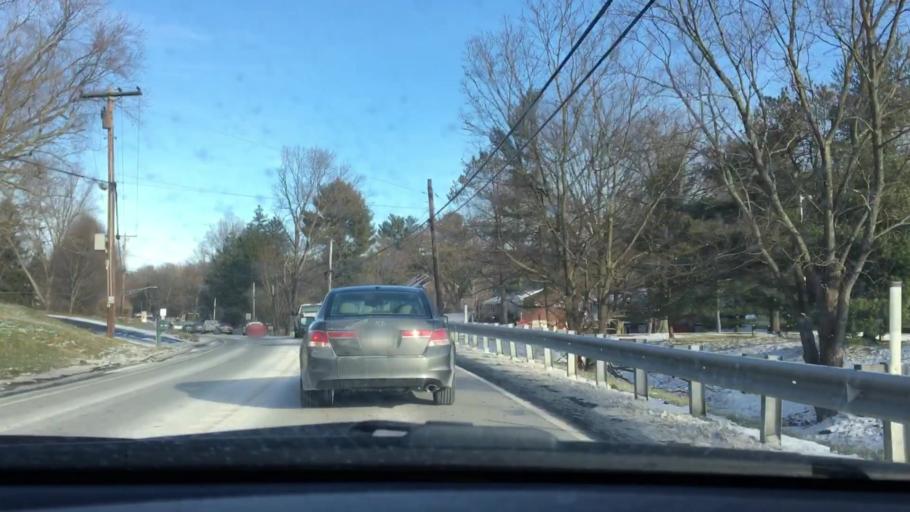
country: US
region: Pennsylvania
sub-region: Washington County
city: Thompsonville
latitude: 40.2694
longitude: -80.1159
